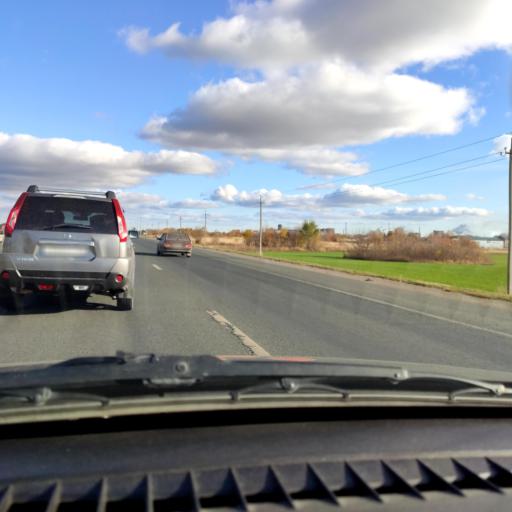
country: RU
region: Samara
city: Tol'yatti
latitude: 53.5756
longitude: 49.4366
